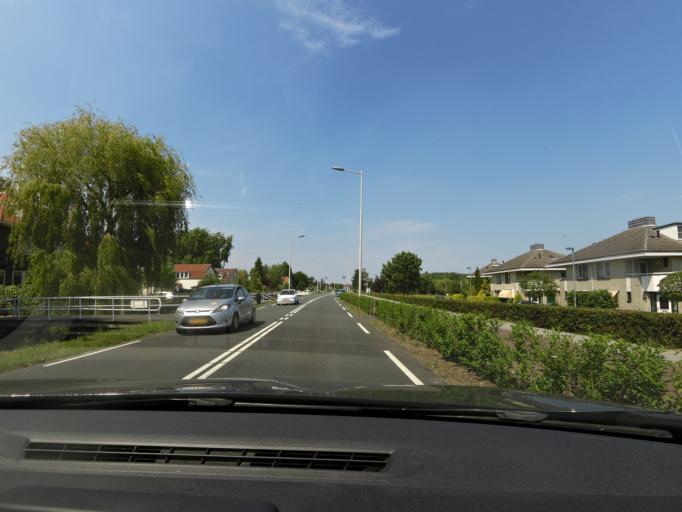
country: NL
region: South Holland
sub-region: Gemeente Lansingerland
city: Bergschenhoek
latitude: 51.9663
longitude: 4.4953
